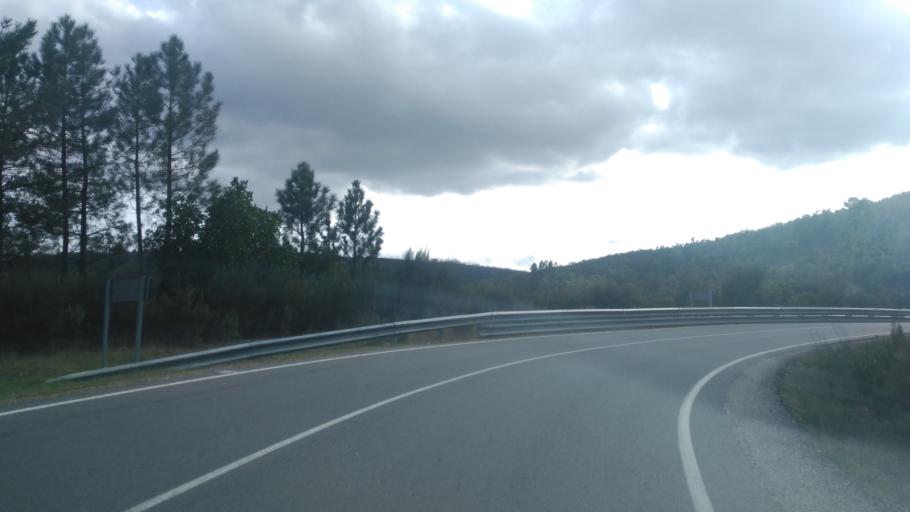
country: ES
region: Castille and Leon
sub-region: Provincia de Salamanca
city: Molinillo
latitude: 40.4885
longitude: -5.9513
